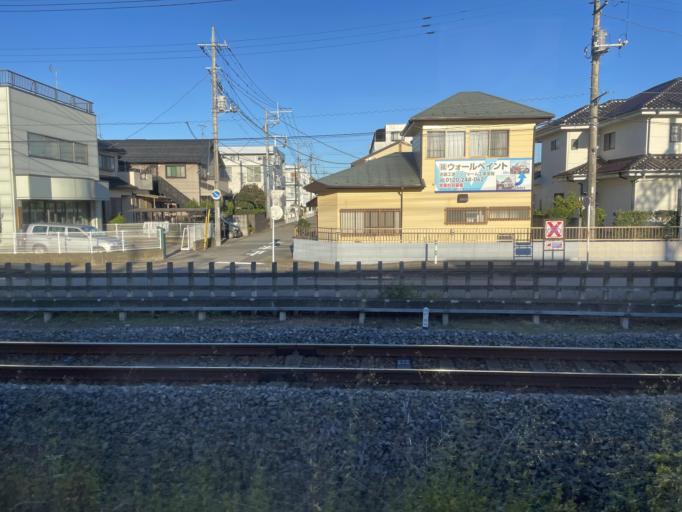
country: JP
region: Saitama
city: Sugito
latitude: 36.0500
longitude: 139.7151
